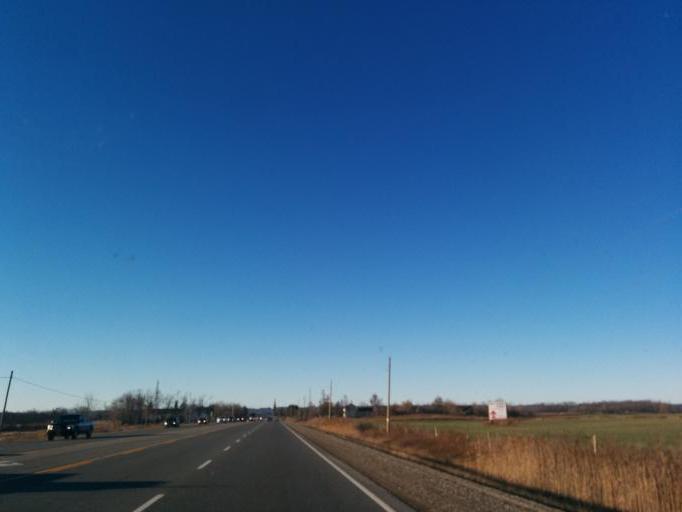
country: CA
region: Ontario
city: Brampton
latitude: 43.7897
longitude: -79.9001
